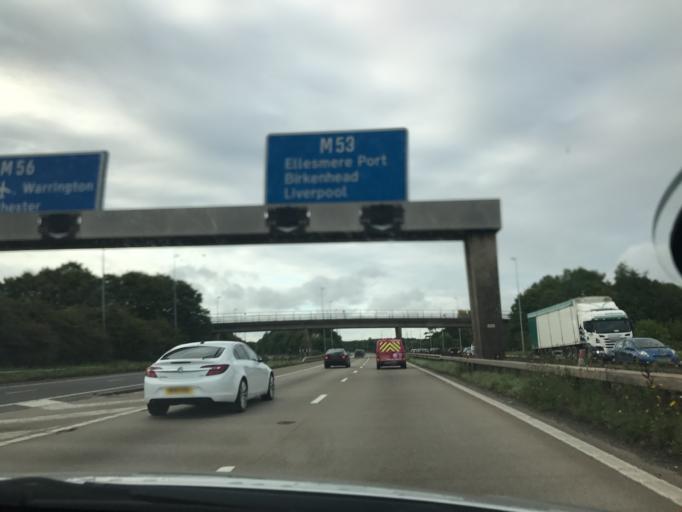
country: GB
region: England
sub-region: Cheshire West and Chester
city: Stoke
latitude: 53.2412
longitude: -2.8640
